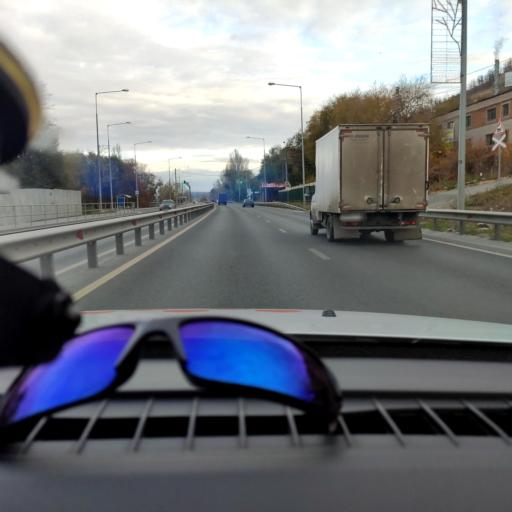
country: RU
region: Samara
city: Volzhskiy
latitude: 53.4019
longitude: 50.1479
